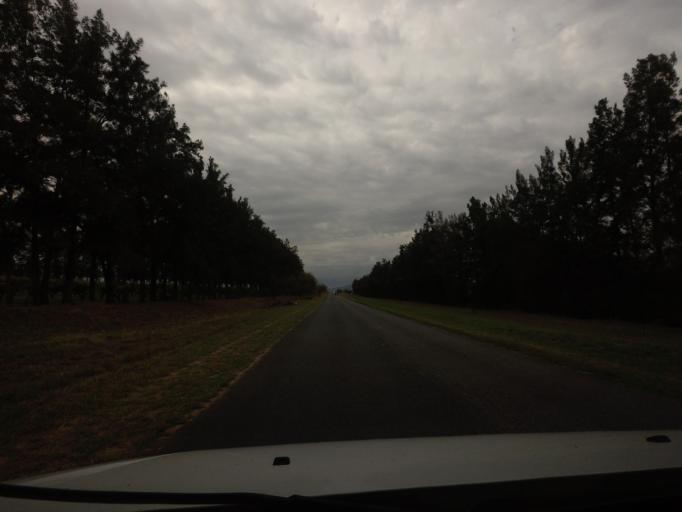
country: ZA
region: Limpopo
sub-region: Mopani District Municipality
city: Hoedspruit
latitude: -24.4432
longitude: 30.8555
